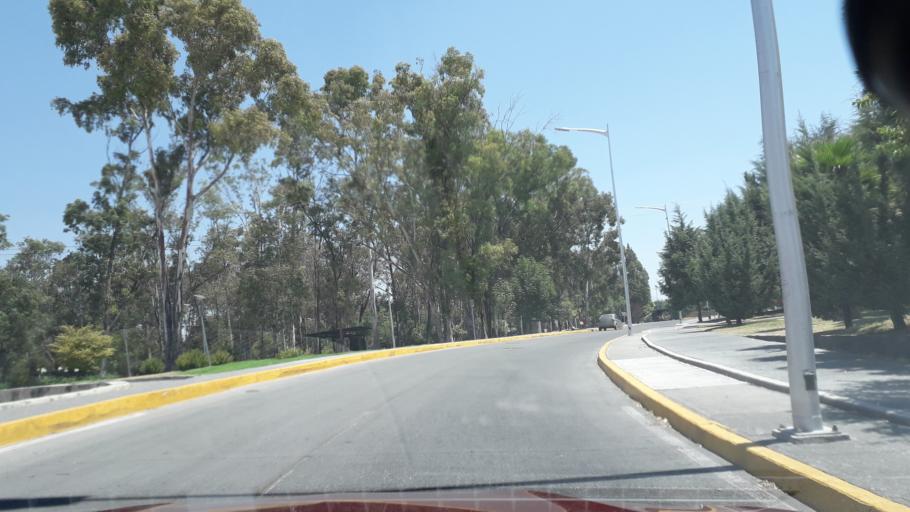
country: MX
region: Puebla
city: Puebla
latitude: 19.0577
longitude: -98.1863
